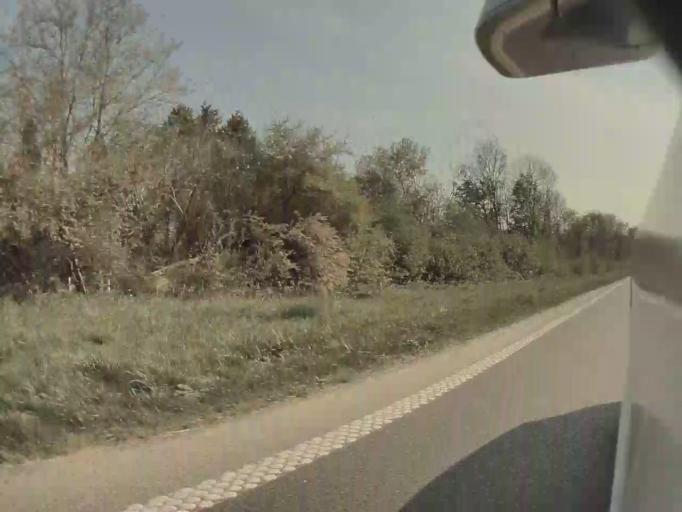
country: BE
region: Wallonia
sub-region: Province de Namur
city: Ciney
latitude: 50.2994
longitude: 5.1194
